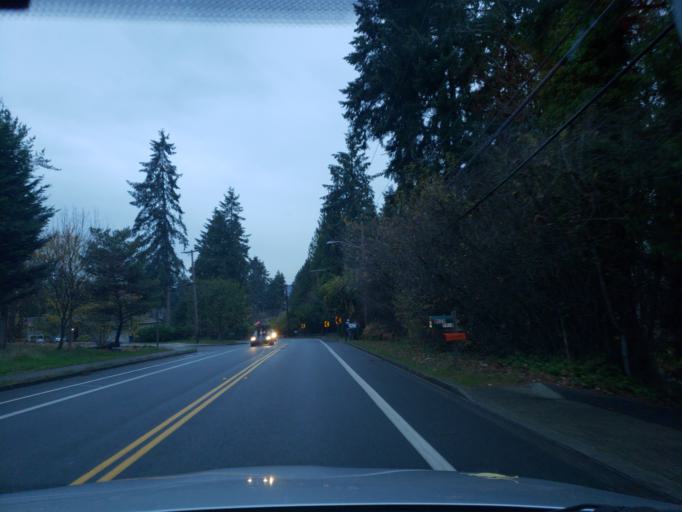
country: US
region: Washington
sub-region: King County
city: Kenmore
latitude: 47.7506
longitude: -122.2354
